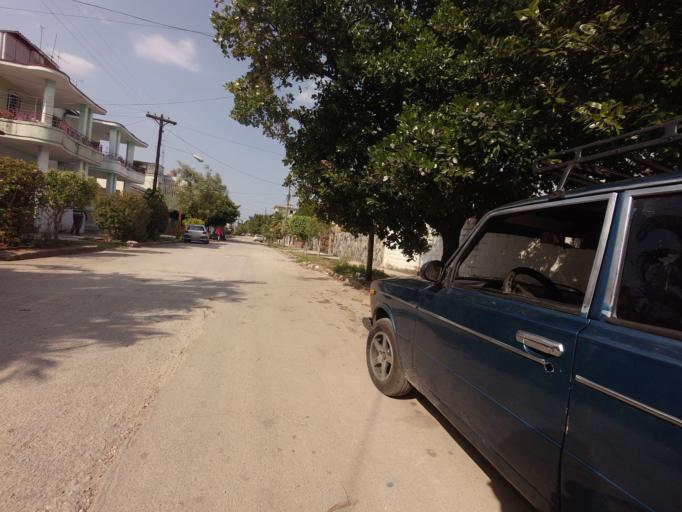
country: CU
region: La Habana
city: Cerro
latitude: 23.1096
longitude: -82.4234
